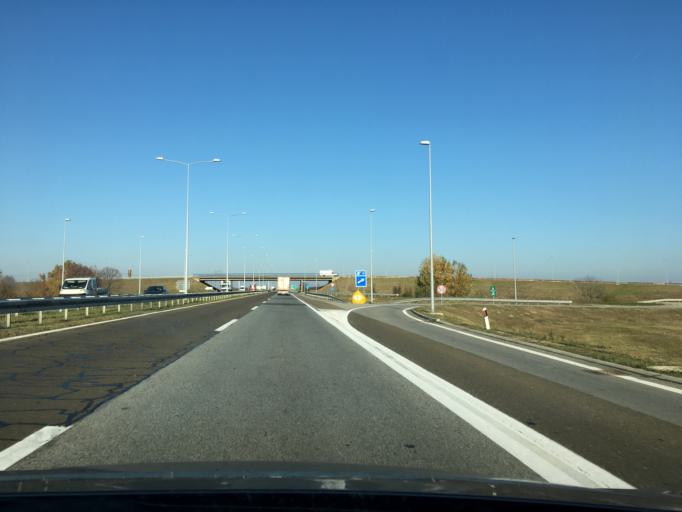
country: RS
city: Novi Karlovci
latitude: 45.0701
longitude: 20.1516
